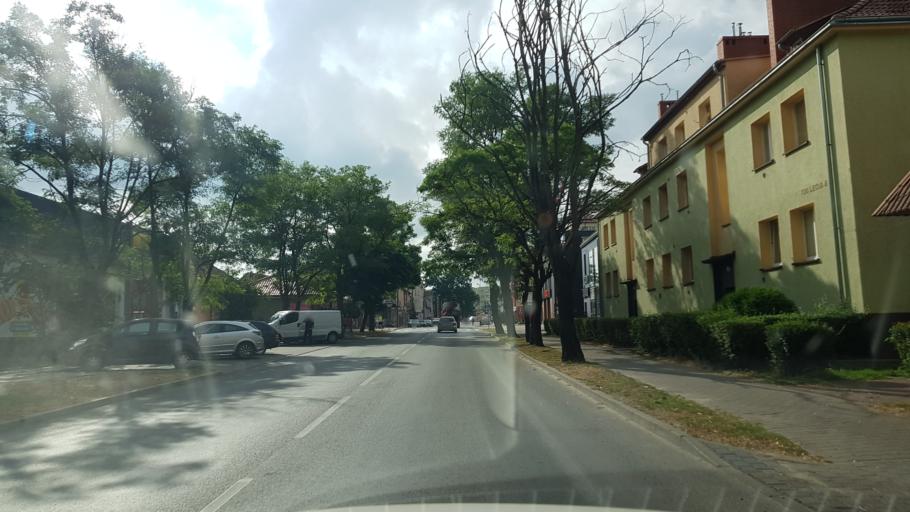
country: PL
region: West Pomeranian Voivodeship
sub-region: Powiat goleniowski
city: Nowogard
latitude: 53.6692
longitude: 15.1231
